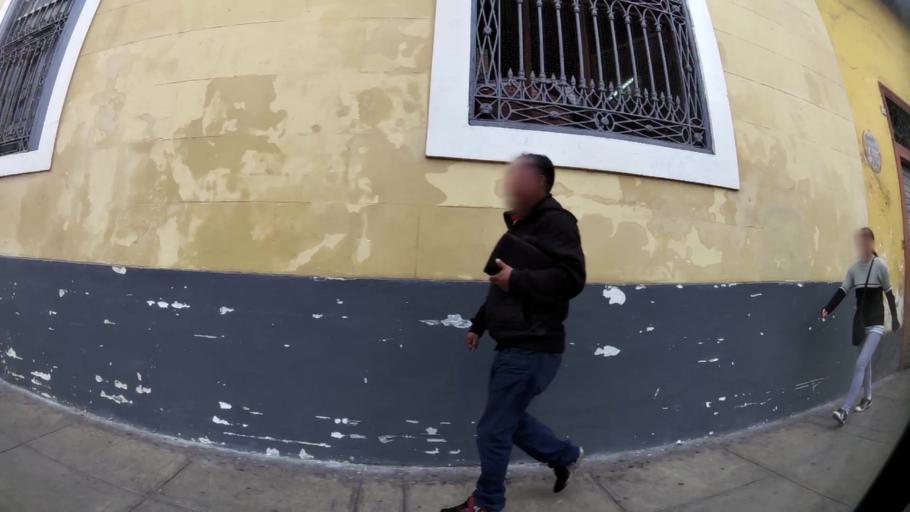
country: PE
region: Lima
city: Lima
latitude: -12.0431
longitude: -77.0329
